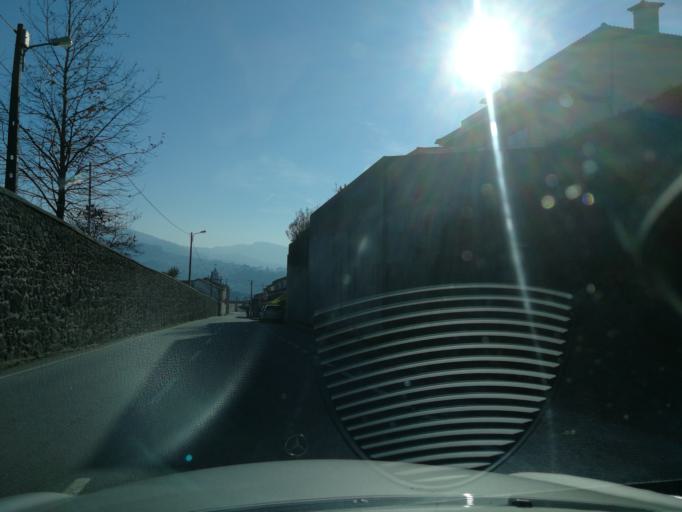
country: PT
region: Braga
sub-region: Braga
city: Adaufe
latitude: 41.5705
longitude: -8.3891
